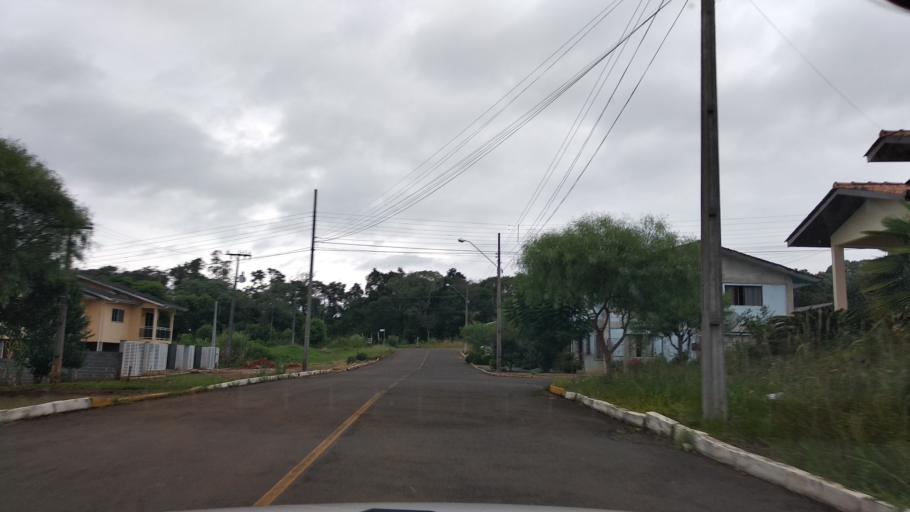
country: BR
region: Santa Catarina
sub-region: Videira
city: Videira
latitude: -26.9857
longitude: -51.1714
